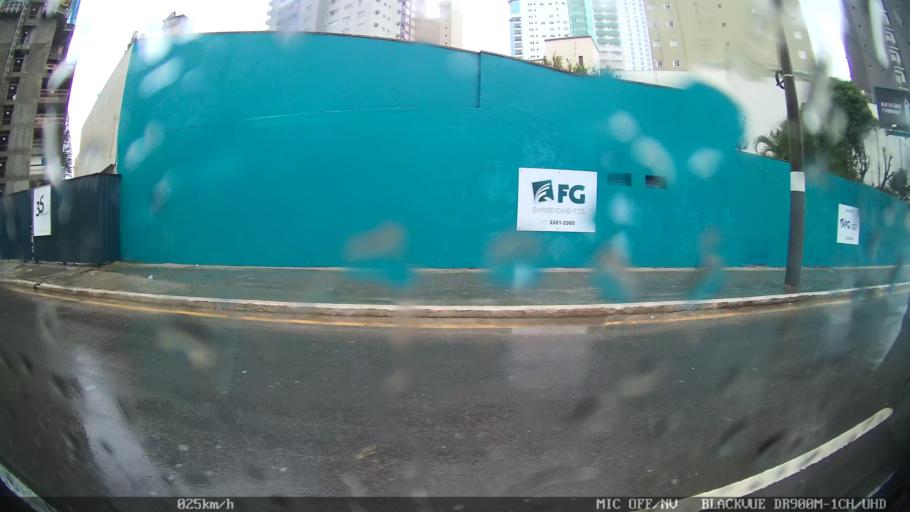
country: BR
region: Santa Catarina
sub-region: Balneario Camboriu
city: Balneario Camboriu
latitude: -27.0048
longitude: -48.6170
